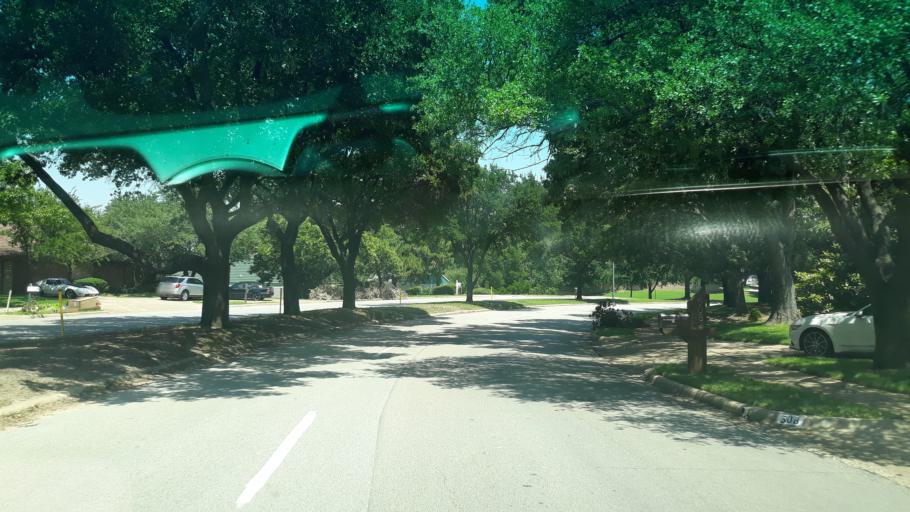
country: US
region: Texas
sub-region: Dallas County
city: Irving
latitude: 32.8547
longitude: -96.9528
